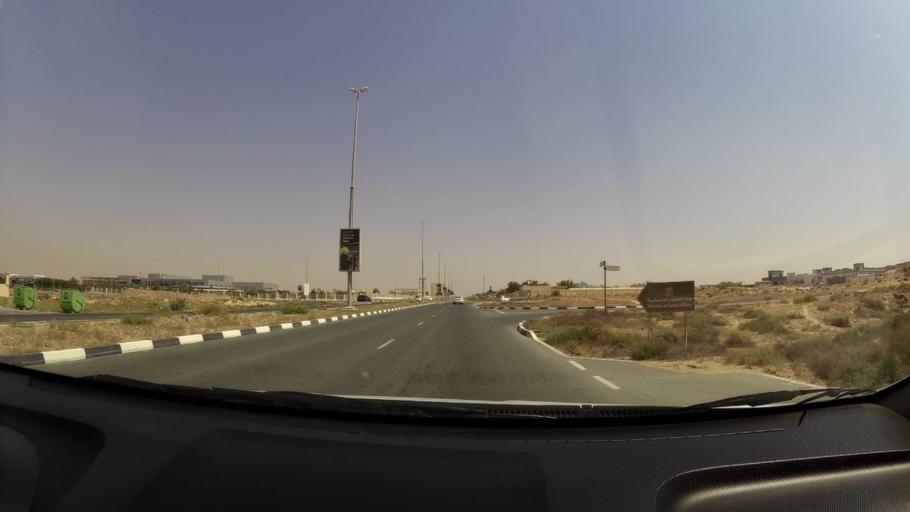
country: AE
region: Umm al Qaywayn
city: Umm al Qaywayn
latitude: 25.5037
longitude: 55.5956
